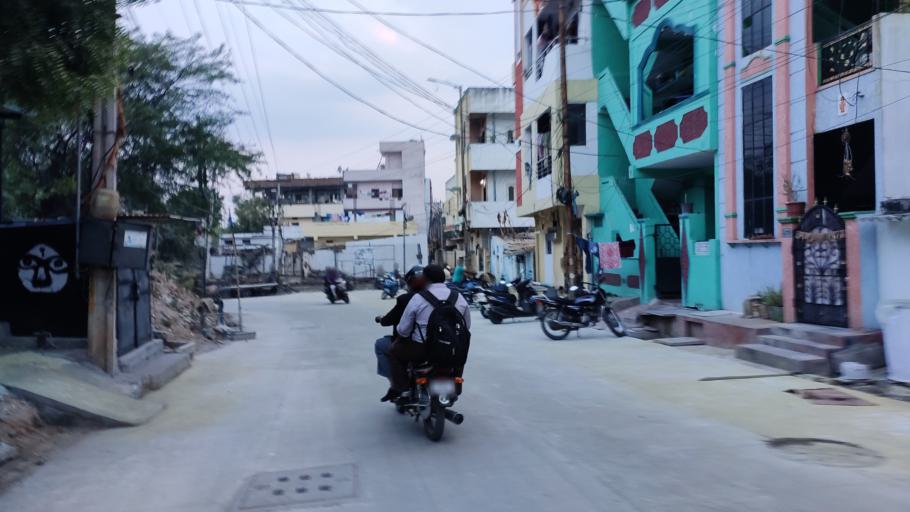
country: IN
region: Telangana
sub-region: Hyderabad
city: Malkajgiri
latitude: 17.4455
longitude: 78.5234
